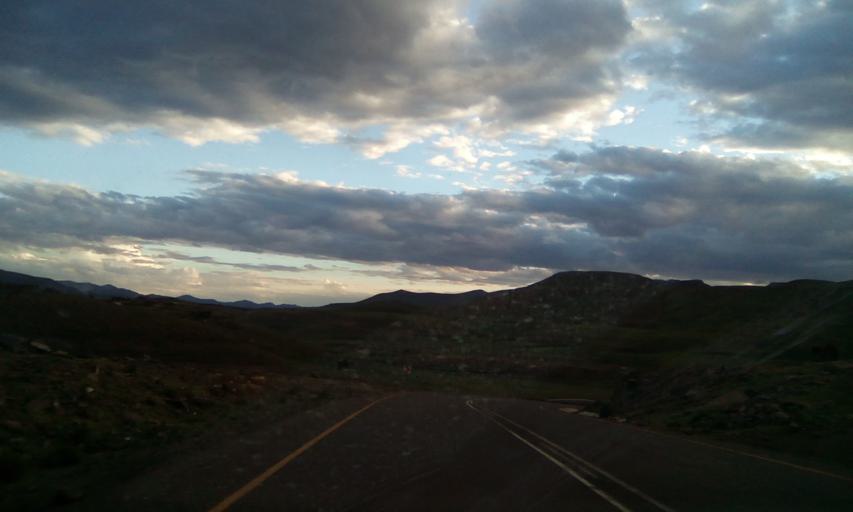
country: LS
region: Maseru
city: Nako
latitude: -29.8019
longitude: 28.0325
